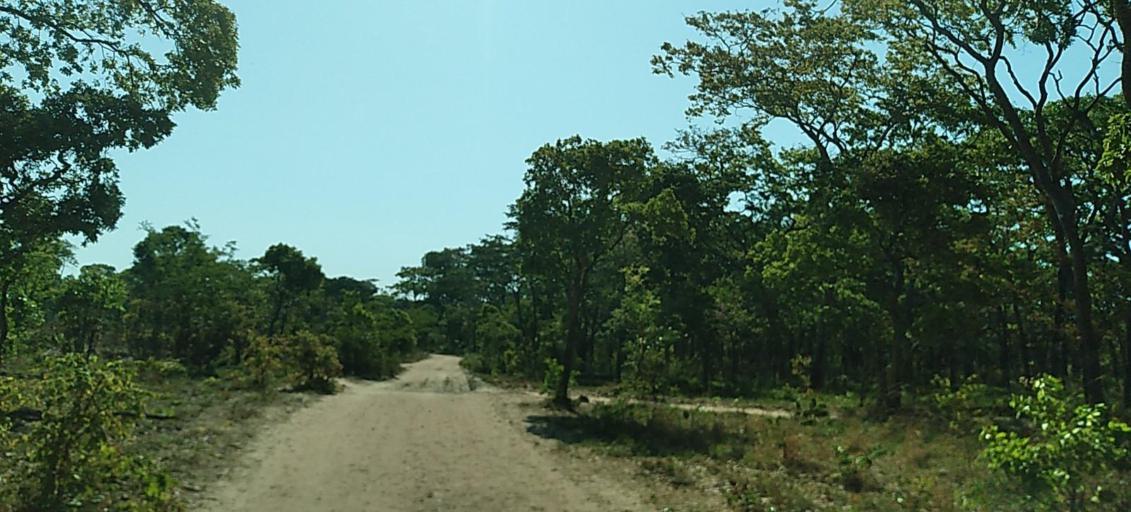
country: ZM
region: Central
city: Mkushi
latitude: -13.4703
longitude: 28.9723
